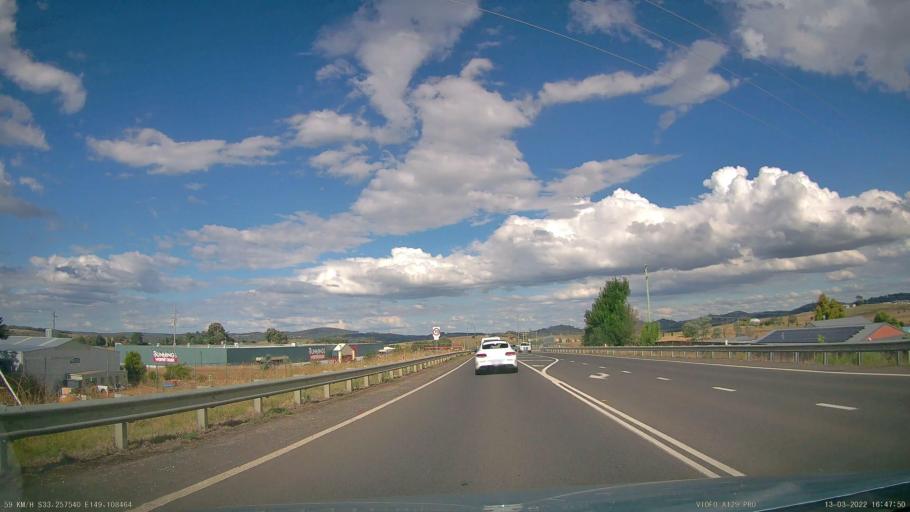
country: AU
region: New South Wales
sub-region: Orange Municipality
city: Orange
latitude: -33.2577
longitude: 149.1085
